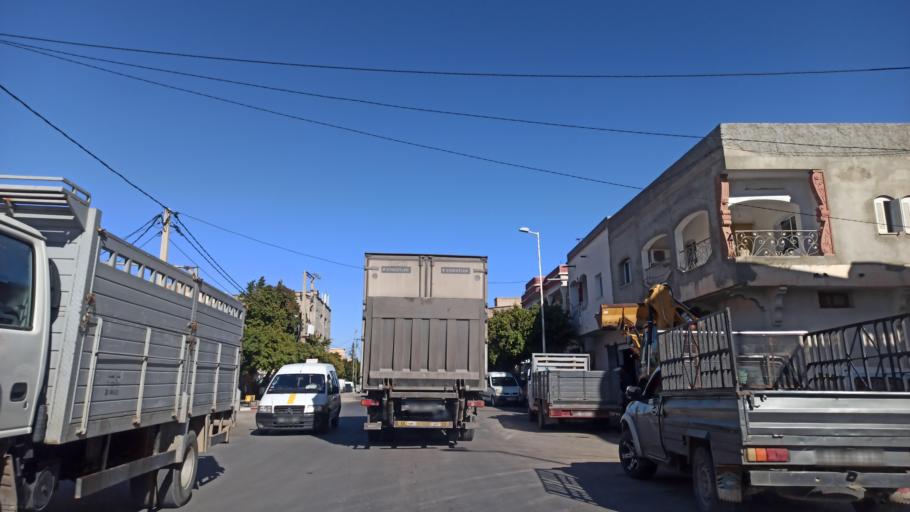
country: TN
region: Sidi Bu Zayd
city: Bi'r al Hufayy
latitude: 34.9343
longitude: 9.1978
